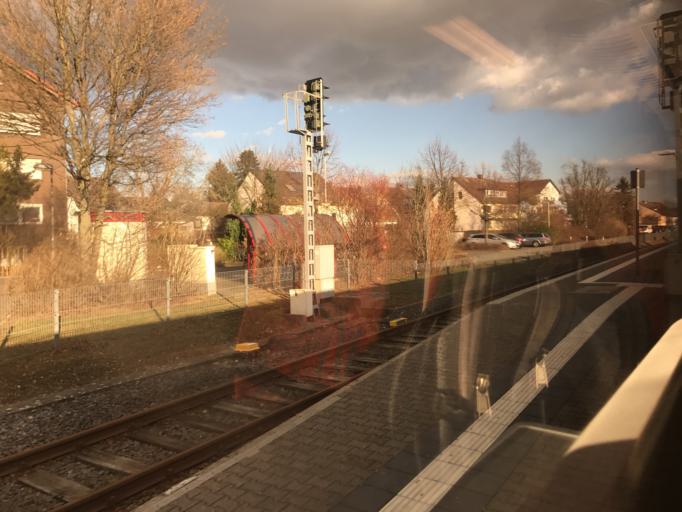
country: DE
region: Hesse
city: Liederbach
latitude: 50.1189
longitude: 8.4853
